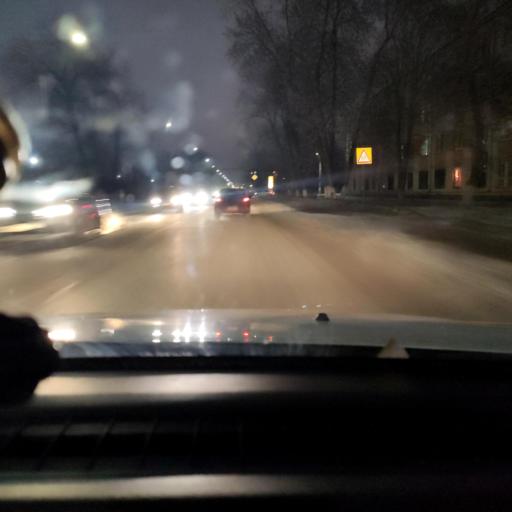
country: RU
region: Samara
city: Chapayevsk
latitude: 52.9726
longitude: 49.7006
